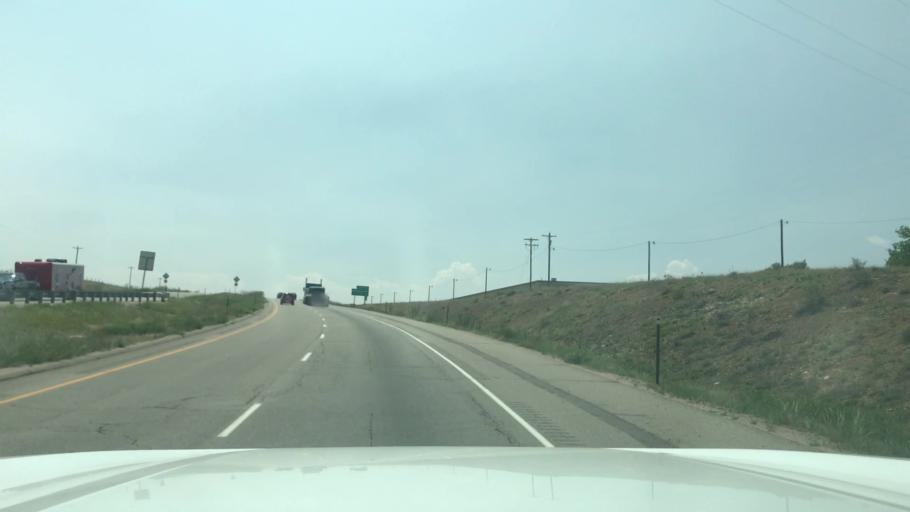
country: US
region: Colorado
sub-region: Pueblo County
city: Colorado City
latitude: 37.9361
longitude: -104.8171
